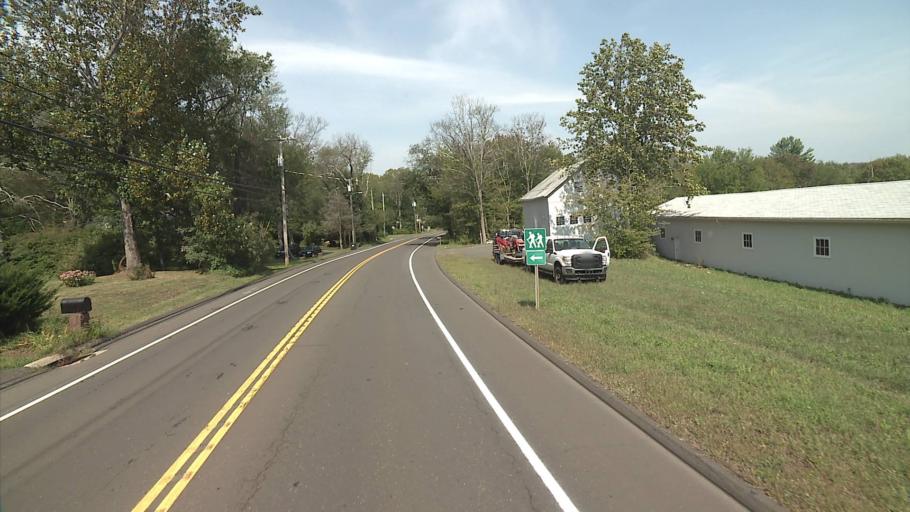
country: US
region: Connecticut
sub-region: Middlesex County
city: Durham
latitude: 41.4105
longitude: -72.6564
